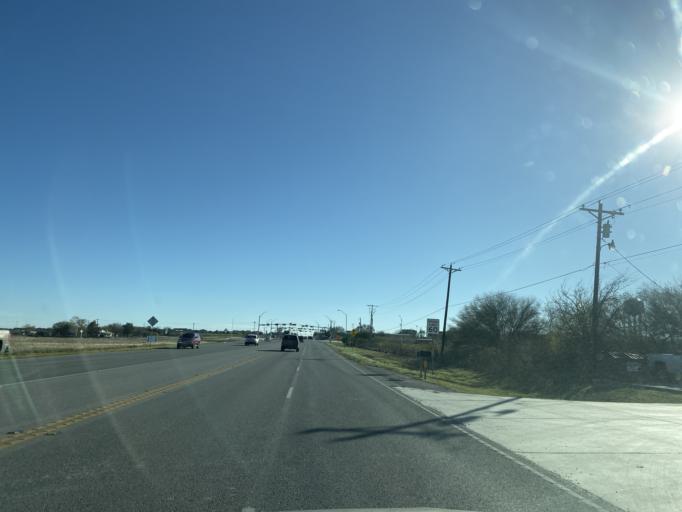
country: US
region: Texas
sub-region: Guadalupe County
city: Redwood
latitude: 29.8327
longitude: -97.9427
